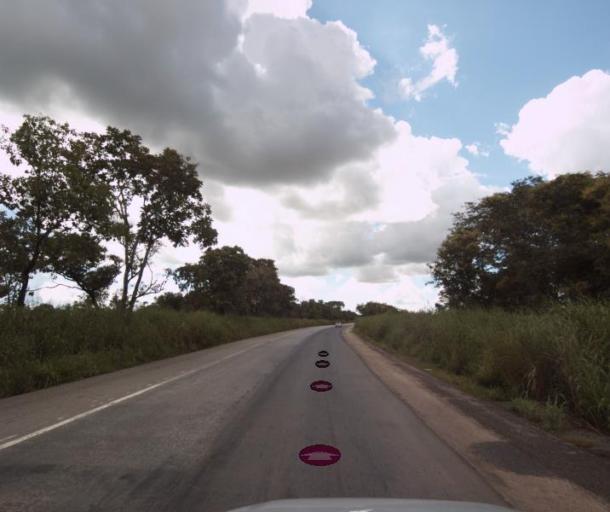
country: BR
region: Goias
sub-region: Porangatu
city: Porangatu
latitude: -13.5488
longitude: -49.1006
